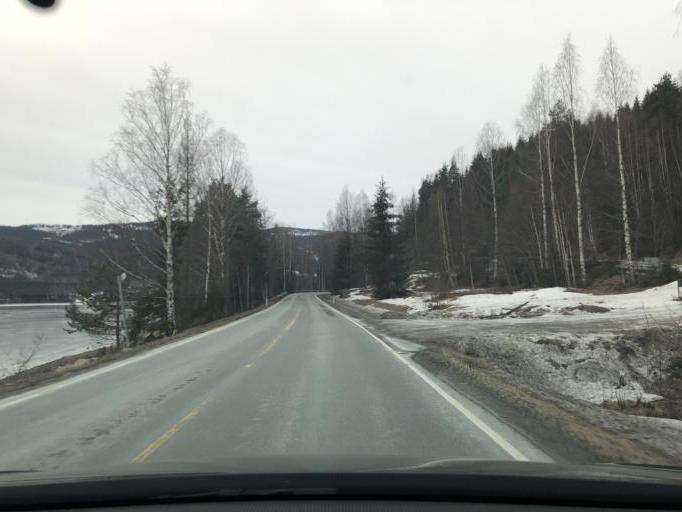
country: NO
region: Buskerud
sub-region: Ringerike
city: Honefoss
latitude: 60.4446
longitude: 10.0787
